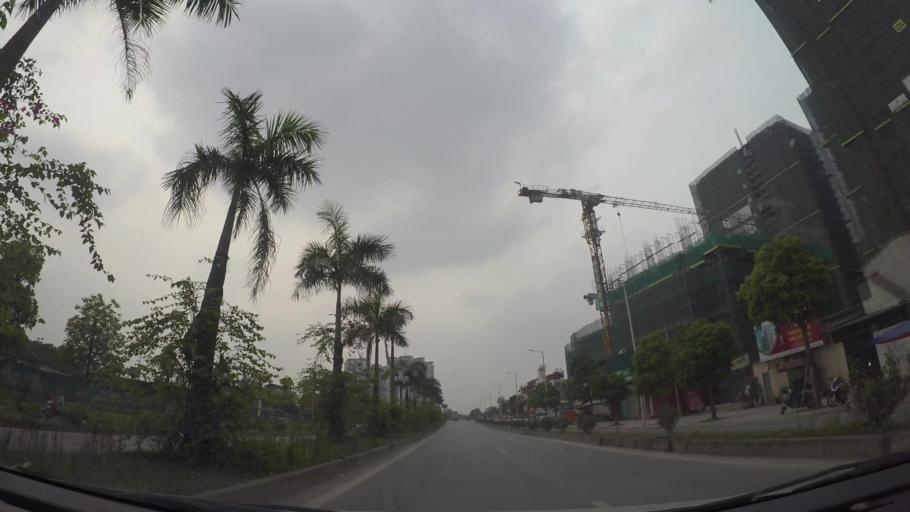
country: VN
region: Ha Noi
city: Cau Dien
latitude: 21.0304
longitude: 105.7605
